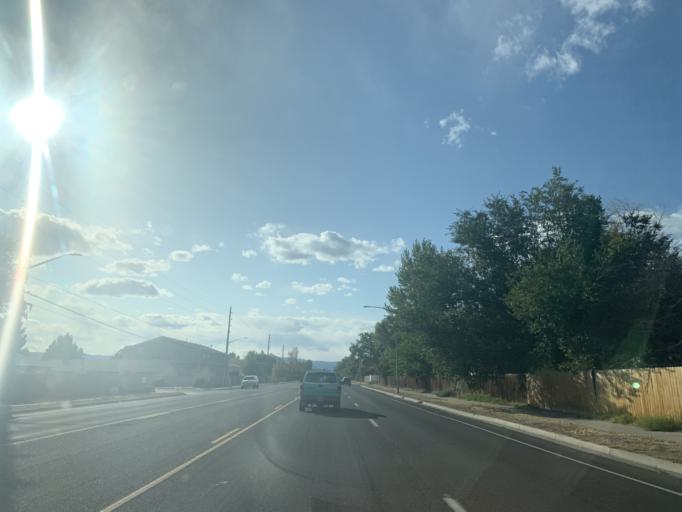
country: US
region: Colorado
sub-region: Mesa County
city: Fruitvale
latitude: 39.0920
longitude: -108.5015
